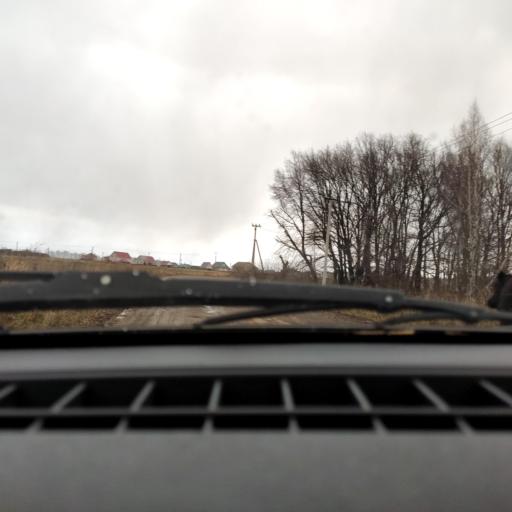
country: RU
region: Bashkortostan
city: Iglino
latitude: 54.7401
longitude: 56.3235
